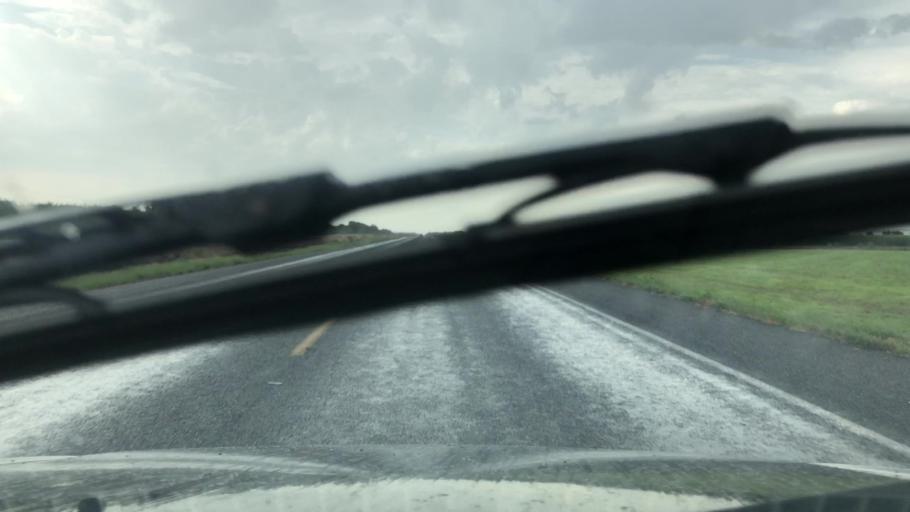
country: US
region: New Mexico
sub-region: Dona Ana County
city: Vado
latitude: 32.1376
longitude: -106.6795
